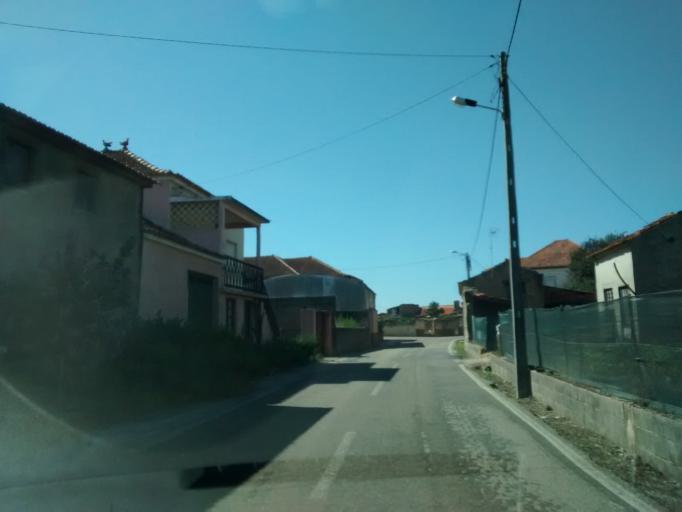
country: PT
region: Aveiro
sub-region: Anadia
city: Sangalhos
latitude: 40.4443
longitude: -8.5057
